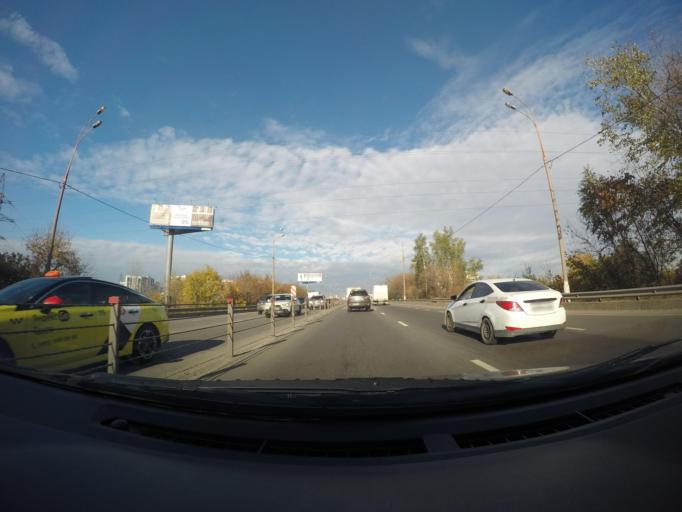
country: RU
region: Moskovskaya
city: Mytishchi
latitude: 55.9173
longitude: 37.7688
